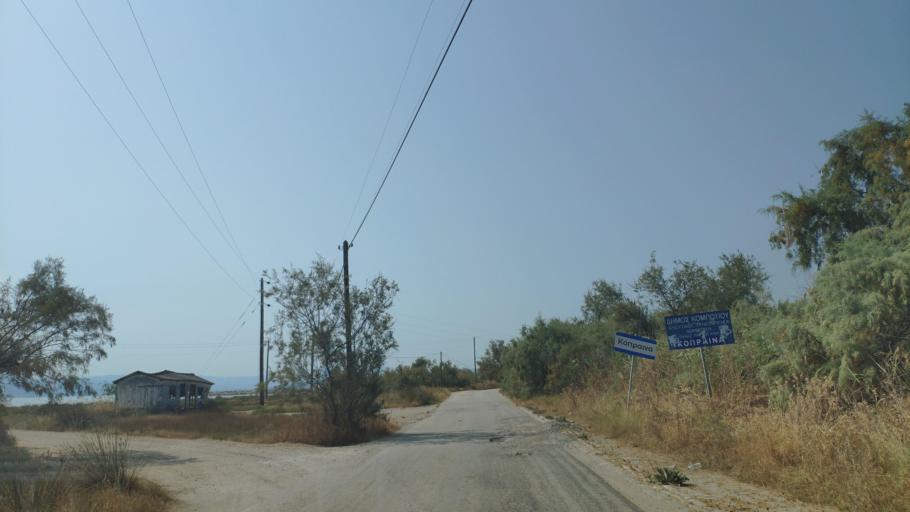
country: GR
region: West Greece
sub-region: Nomos Aitolias kai Akarnanias
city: Menidi
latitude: 39.0413
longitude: 21.0744
